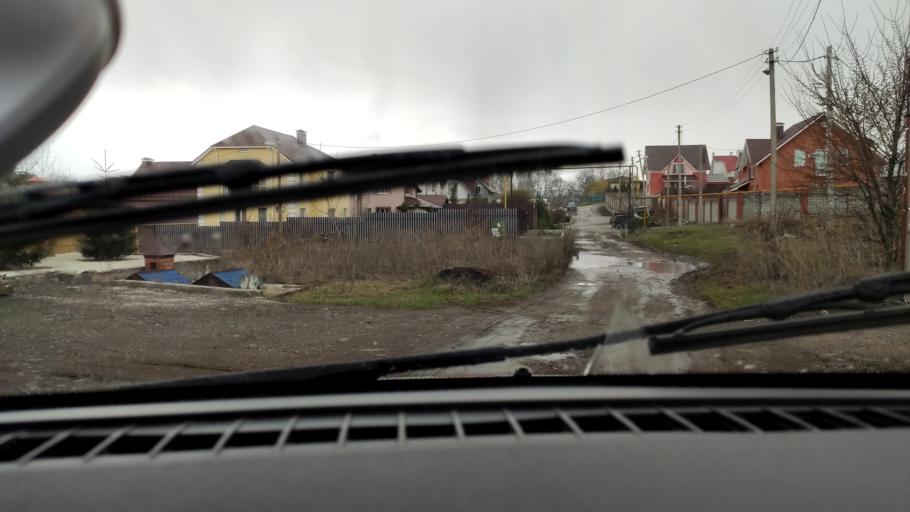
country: RU
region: Samara
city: Novosemeykino
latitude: 53.3299
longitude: 50.2889
